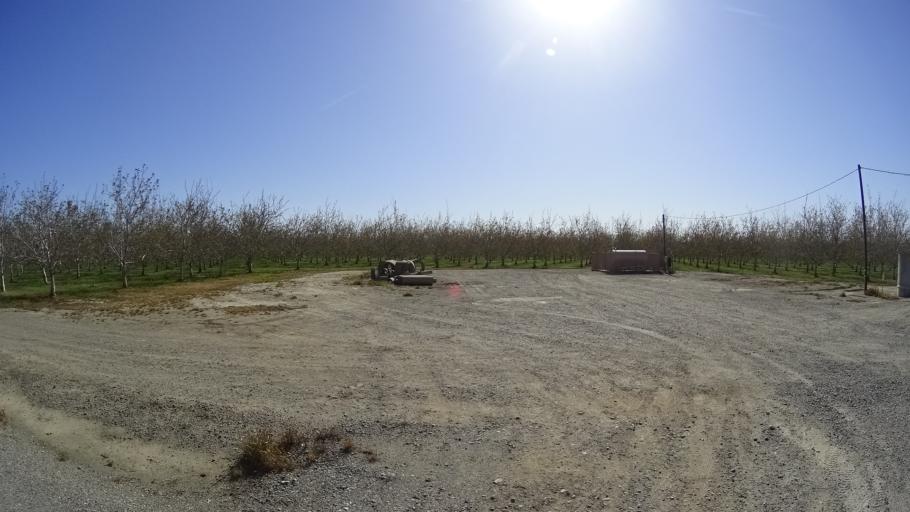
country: US
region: California
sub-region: Glenn County
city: Hamilton City
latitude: 39.6918
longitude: -122.0742
